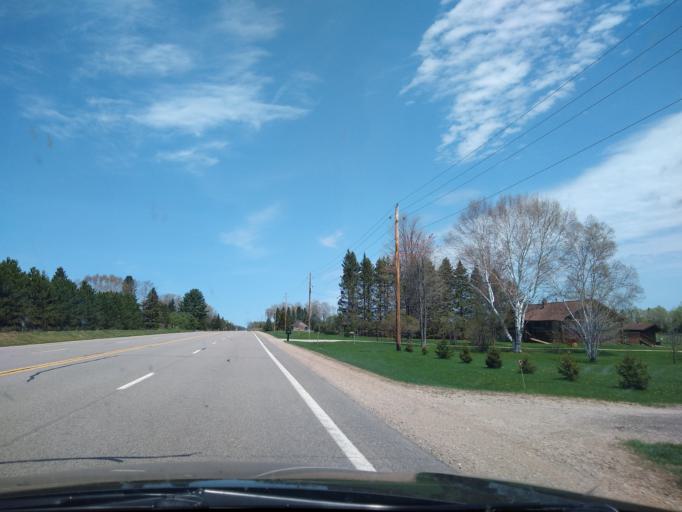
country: US
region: Michigan
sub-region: Delta County
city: Gladstone
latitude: 46.0831
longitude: -86.9808
